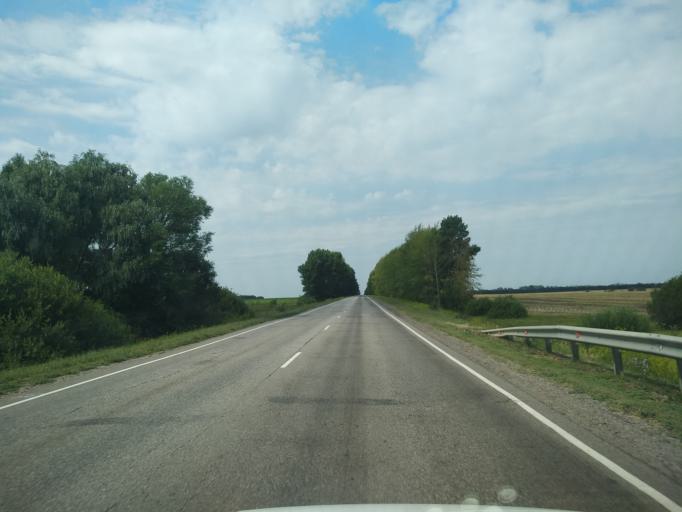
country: RU
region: Voronezj
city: Pereleshino
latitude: 51.7312
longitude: 40.0610
